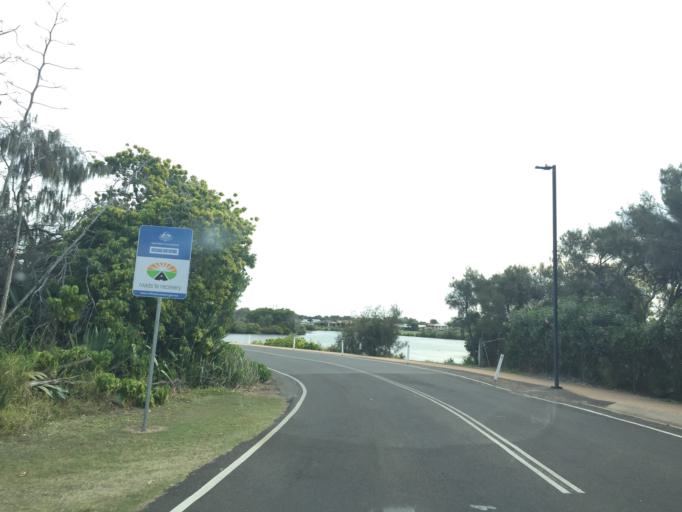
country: AU
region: Queensland
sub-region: Bundaberg
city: Bundaberg
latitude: -24.8253
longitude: 152.4646
